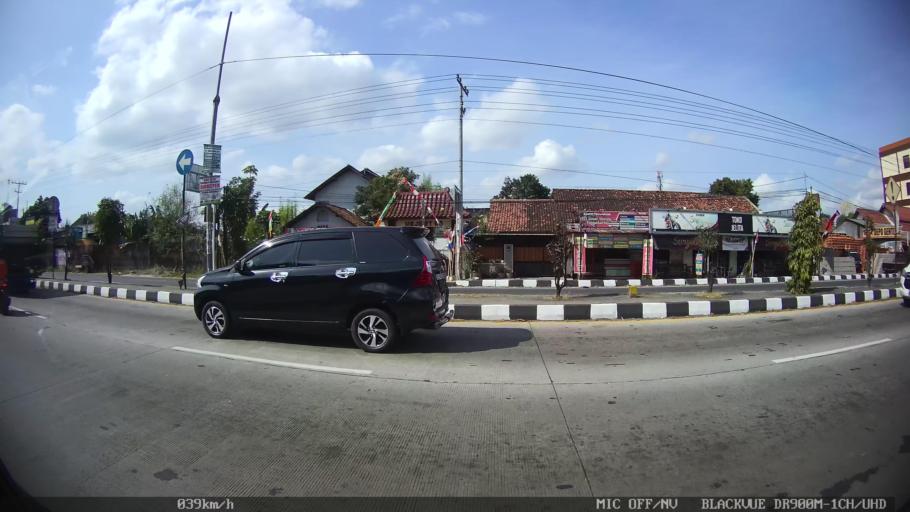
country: ID
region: Daerah Istimewa Yogyakarta
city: Sewon
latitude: -7.8364
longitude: 110.3733
